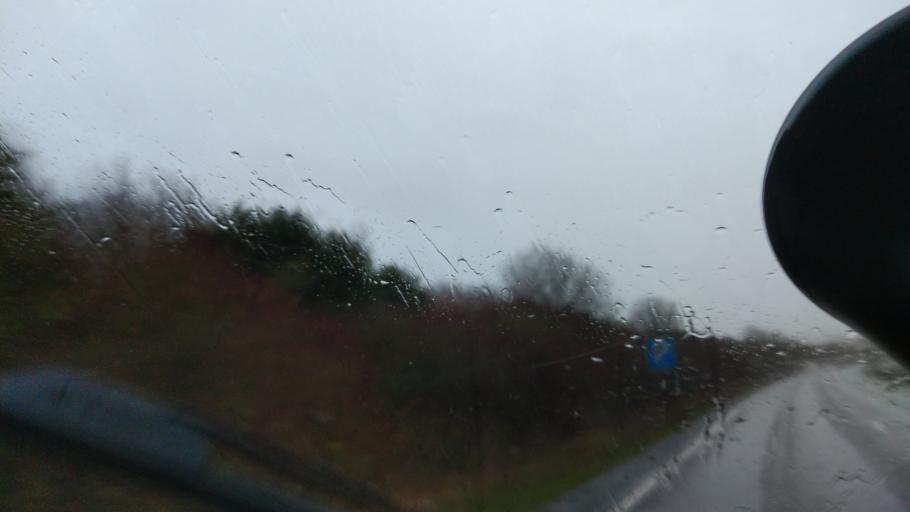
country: GB
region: England
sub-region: East Sussex
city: Portslade
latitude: 50.8487
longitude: -0.2445
